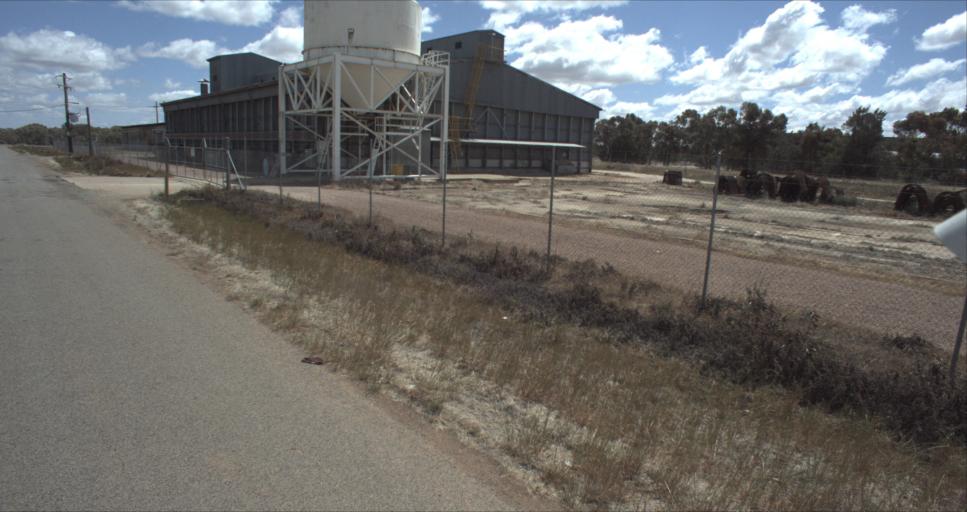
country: AU
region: New South Wales
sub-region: Murrumbidgee Shire
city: Darlington Point
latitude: -34.5155
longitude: 146.1788
